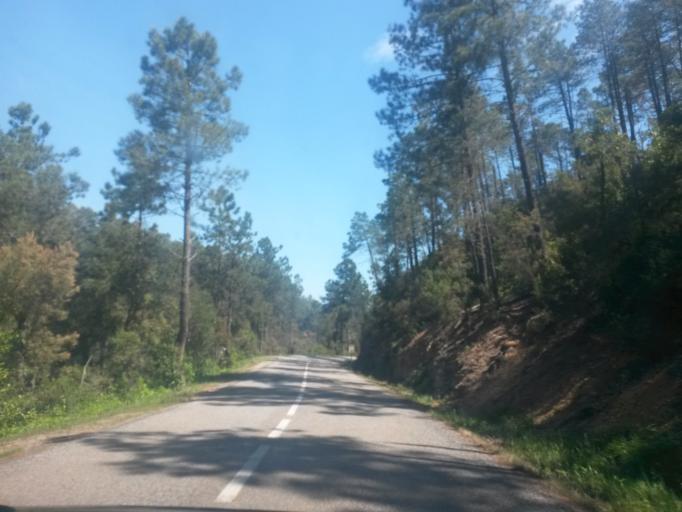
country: ES
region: Catalonia
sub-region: Provincia de Girona
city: Madremanya
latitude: 41.9826
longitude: 2.9452
